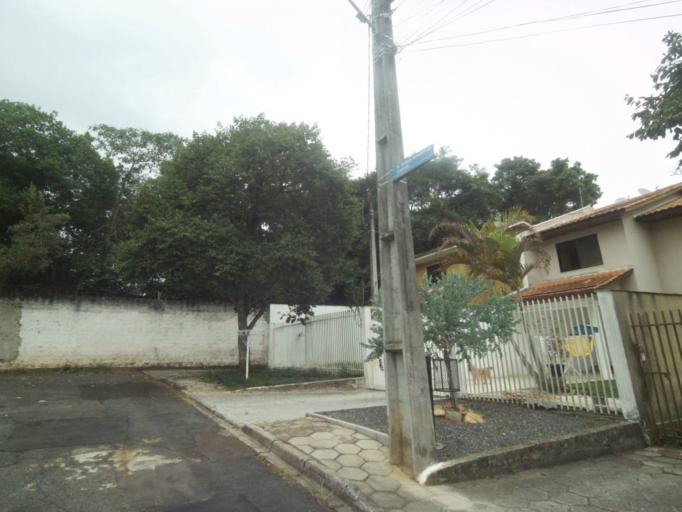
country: BR
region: Parana
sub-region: Curitiba
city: Curitiba
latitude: -25.3854
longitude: -49.2918
